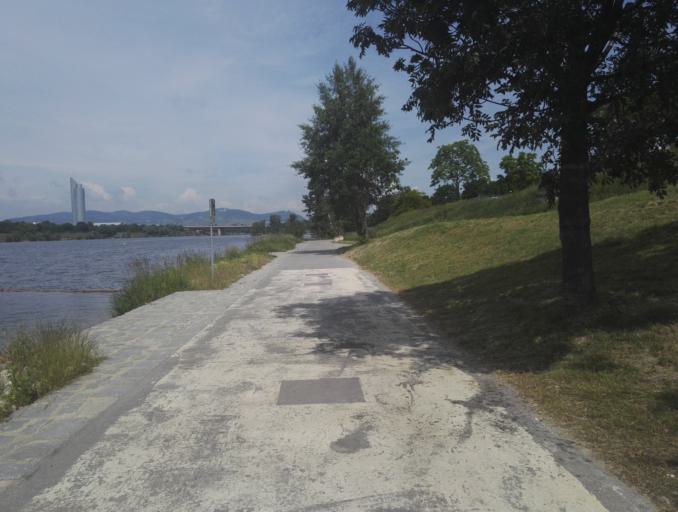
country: AT
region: Vienna
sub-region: Wien Stadt
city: Vienna
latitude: 48.2328
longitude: 16.4086
